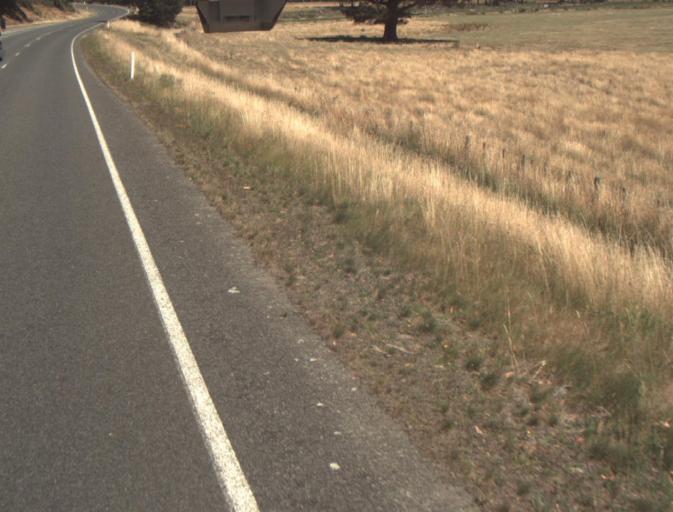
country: AU
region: Tasmania
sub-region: Dorset
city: Scottsdale
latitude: -41.3178
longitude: 147.3655
